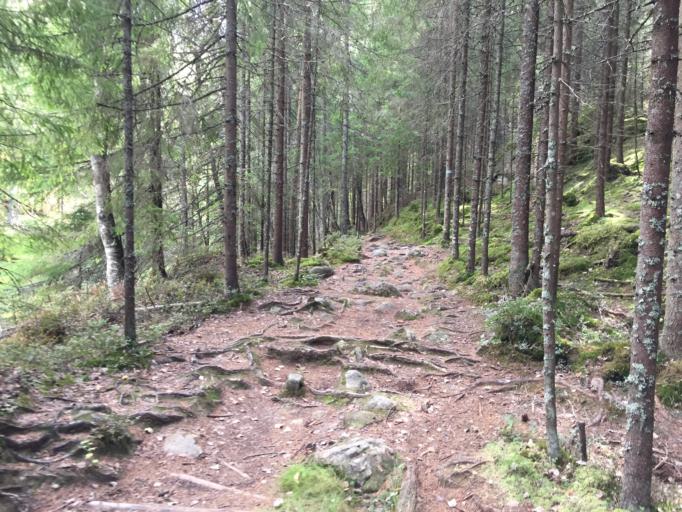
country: NO
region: Akershus
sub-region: Raelingen
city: Fjerdingby
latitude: 59.9084
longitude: 11.0299
